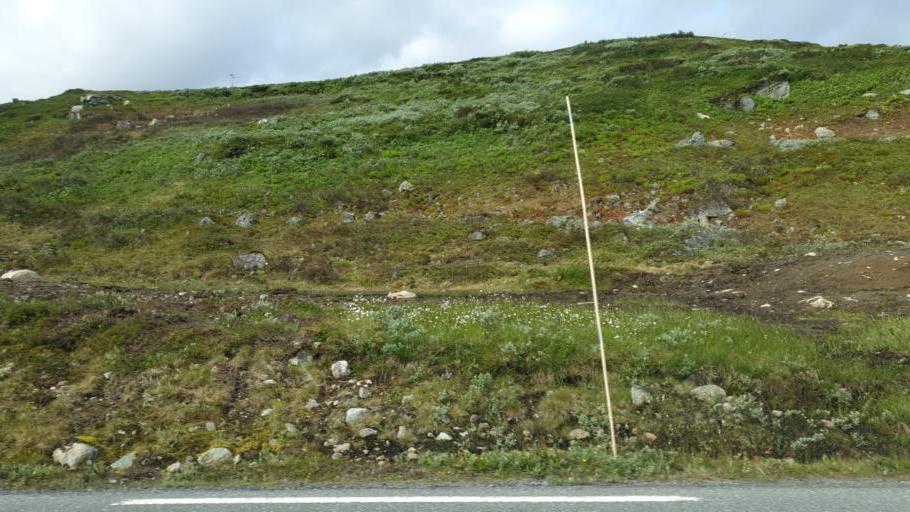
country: NO
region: Oppland
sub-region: Vestre Slidre
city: Slidre
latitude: 61.3201
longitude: 8.8056
